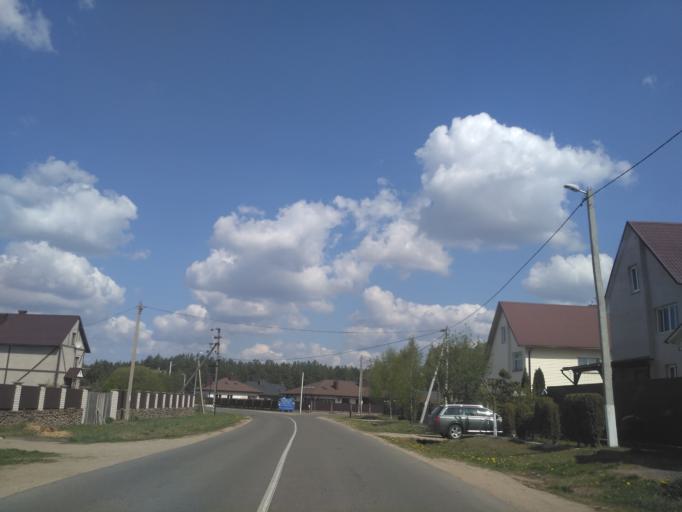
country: BY
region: Minsk
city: Radashkovichy
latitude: 54.1677
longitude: 27.2464
